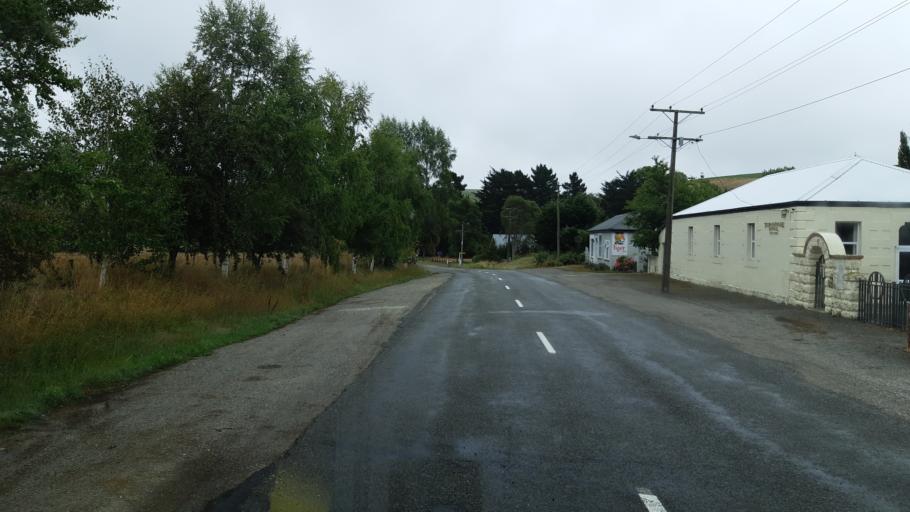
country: NZ
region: Otago
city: Oamaru
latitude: -44.9615
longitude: 170.6442
